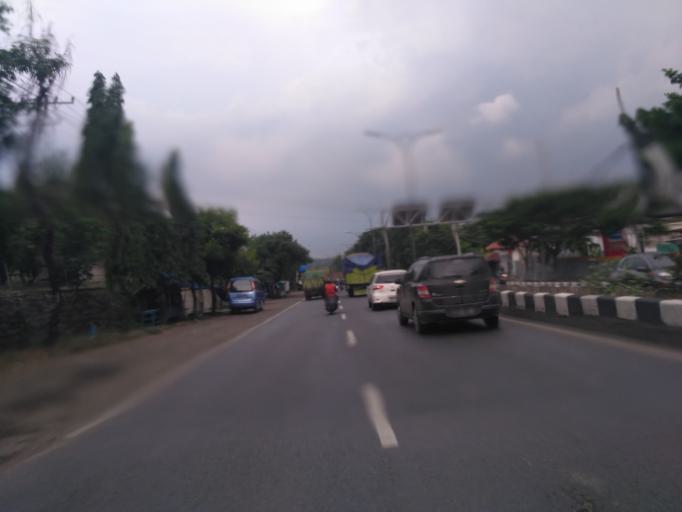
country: ID
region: Central Java
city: Semarang
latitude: -6.9709
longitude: 110.2918
